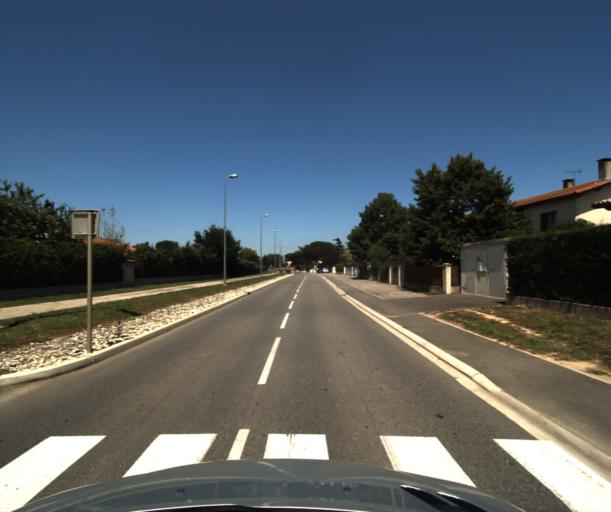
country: FR
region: Midi-Pyrenees
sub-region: Departement de la Haute-Garonne
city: Roquettes
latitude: 43.4929
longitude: 1.3785
